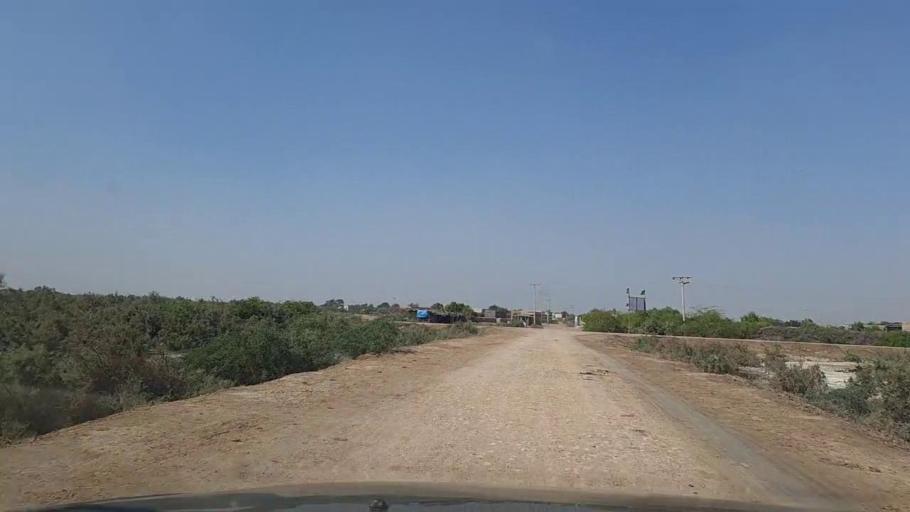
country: PK
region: Sindh
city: Daro Mehar
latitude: 24.8368
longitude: 68.1398
